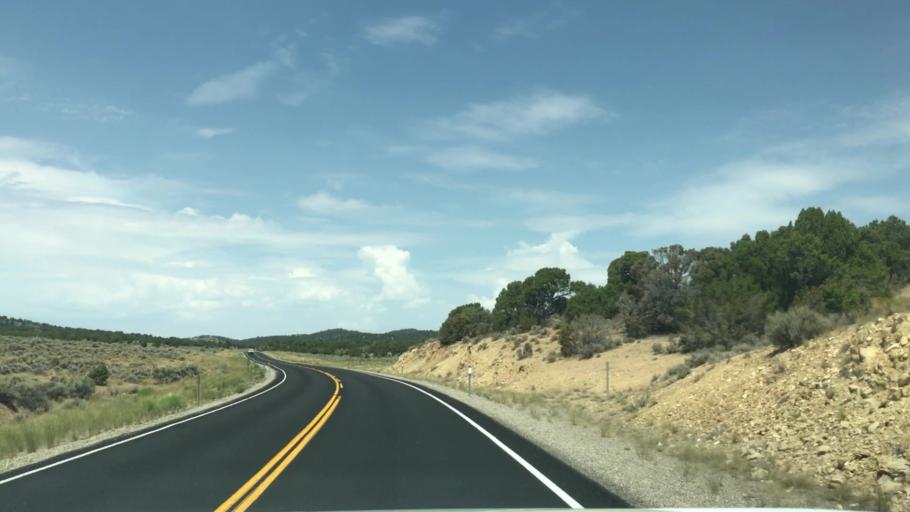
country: US
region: Nevada
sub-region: Eureka County
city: Eureka
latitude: 39.3889
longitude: -115.4491
